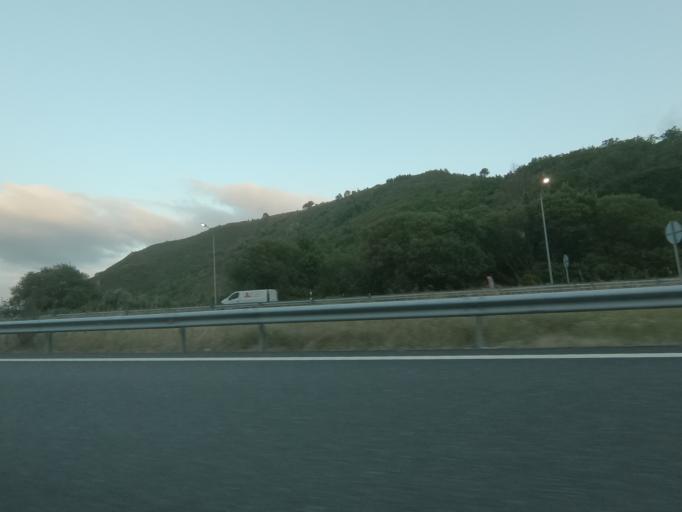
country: ES
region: Galicia
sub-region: Provincia de Pontevedra
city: Covelo
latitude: 42.1801
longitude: -8.3369
